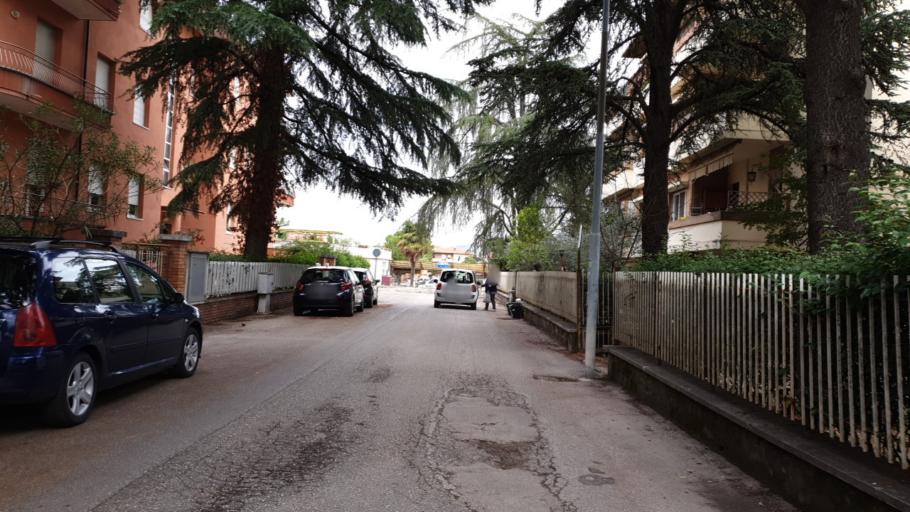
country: IT
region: Umbria
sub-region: Provincia di Perugia
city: Foligno
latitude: 42.9613
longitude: 12.7114
